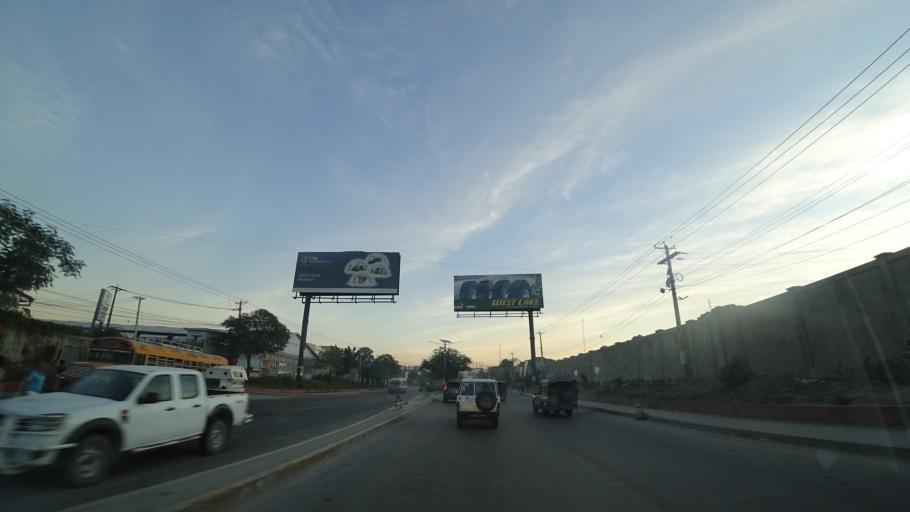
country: HT
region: Ouest
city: Delmas 73
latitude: 18.5683
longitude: -72.3107
